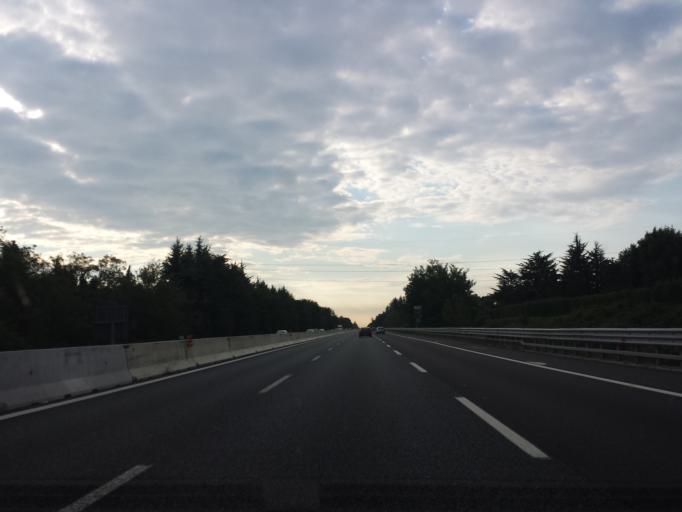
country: IT
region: Lombardy
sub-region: Provincia di Varese
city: Olgiate Olona
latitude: 45.6358
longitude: 8.8671
